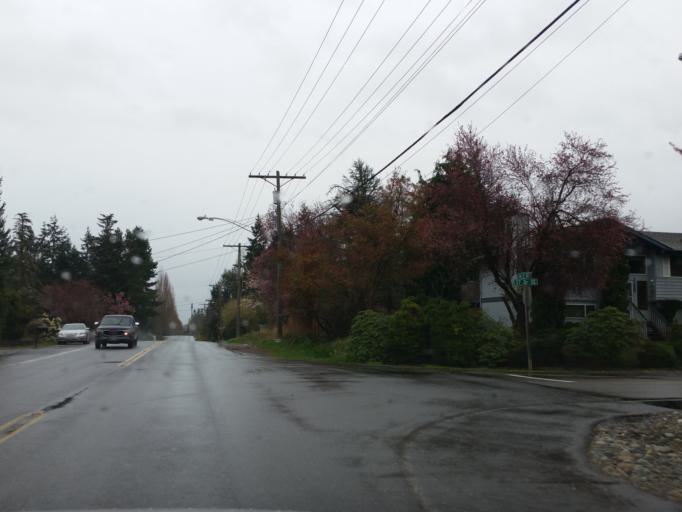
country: US
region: Washington
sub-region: Snohomish County
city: Silver Firs
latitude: 47.8924
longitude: -122.1824
